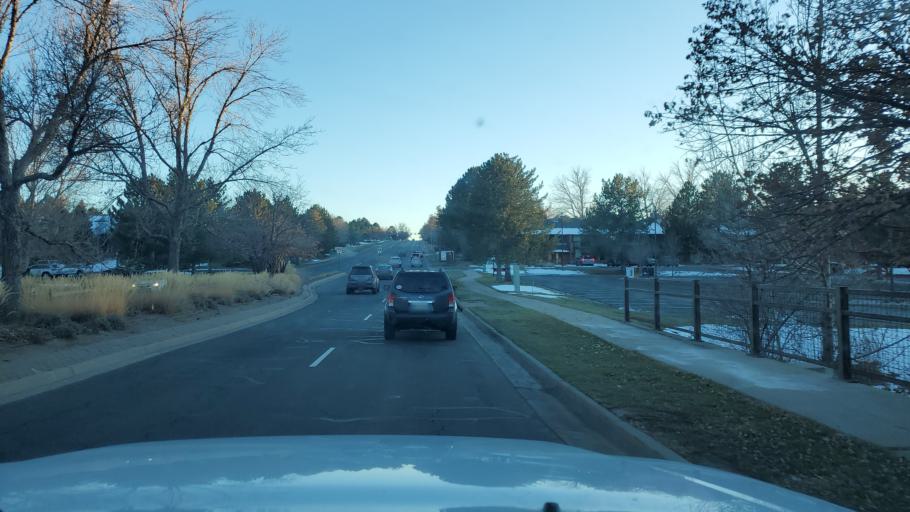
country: US
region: Colorado
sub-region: Arapahoe County
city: Castlewood
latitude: 39.6078
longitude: -104.9042
